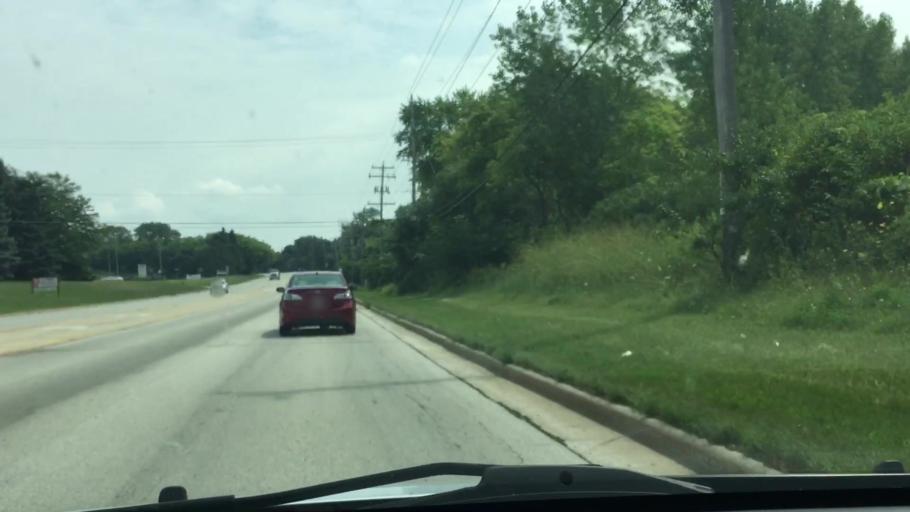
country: US
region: Wisconsin
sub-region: Waukesha County
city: Waukesha
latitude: 43.0371
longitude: -88.2014
